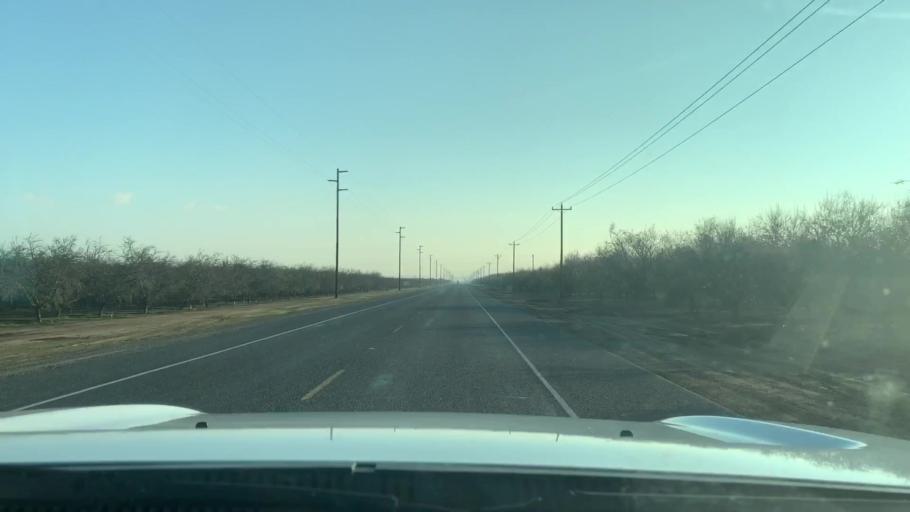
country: US
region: California
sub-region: Kern County
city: Wasco
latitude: 35.6011
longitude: -119.4675
